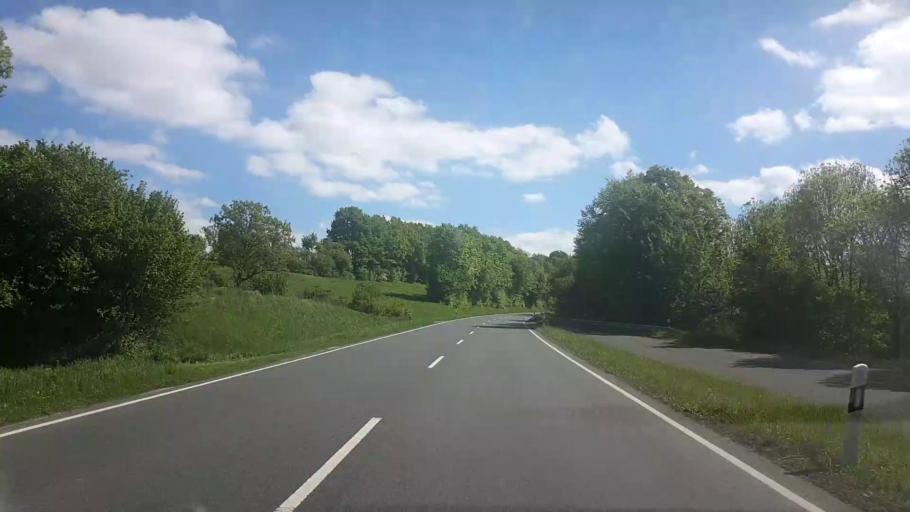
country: DE
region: Bavaria
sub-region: Upper Franconia
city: Rattelsdorf
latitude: 50.0593
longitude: 10.8776
